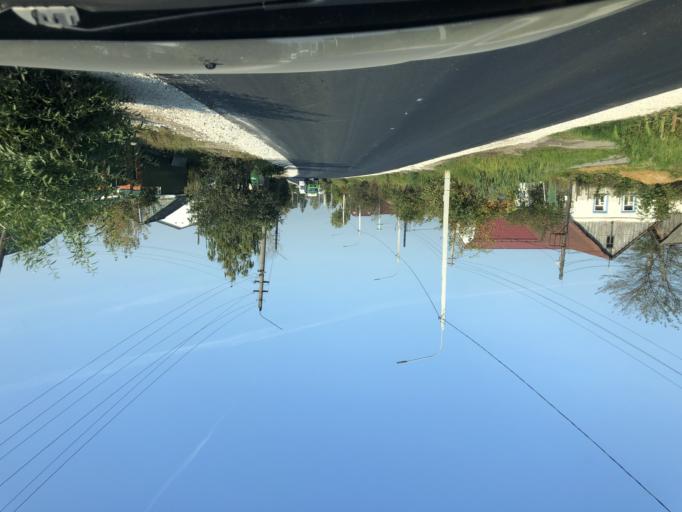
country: RU
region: Tula
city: Leninskiy
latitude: 54.2895
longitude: 37.4650
